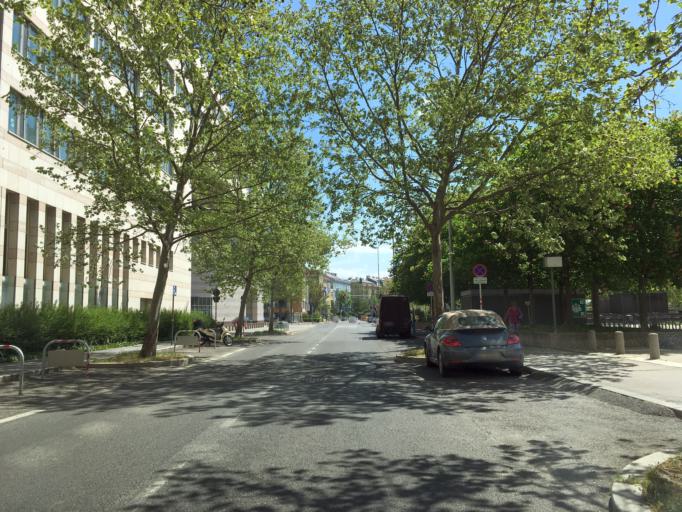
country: AT
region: Vienna
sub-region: Wien Stadt
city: Vienna
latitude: 48.2215
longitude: 16.3945
